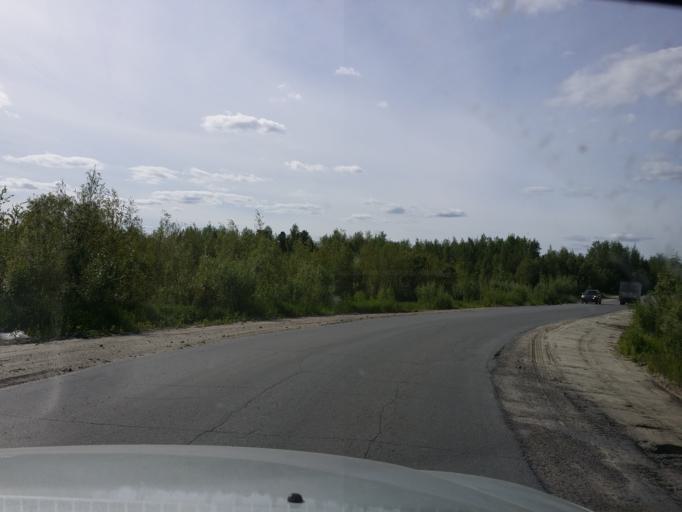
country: RU
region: Khanty-Mansiyskiy Avtonomnyy Okrug
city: Nizhnevartovsk
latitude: 60.9993
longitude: 76.5633
